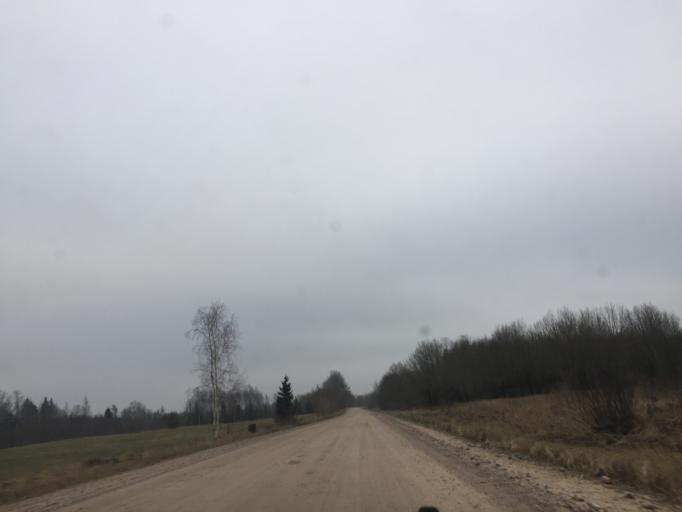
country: LV
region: Limbazu Rajons
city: Limbazi
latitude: 57.6009
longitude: 24.6134
